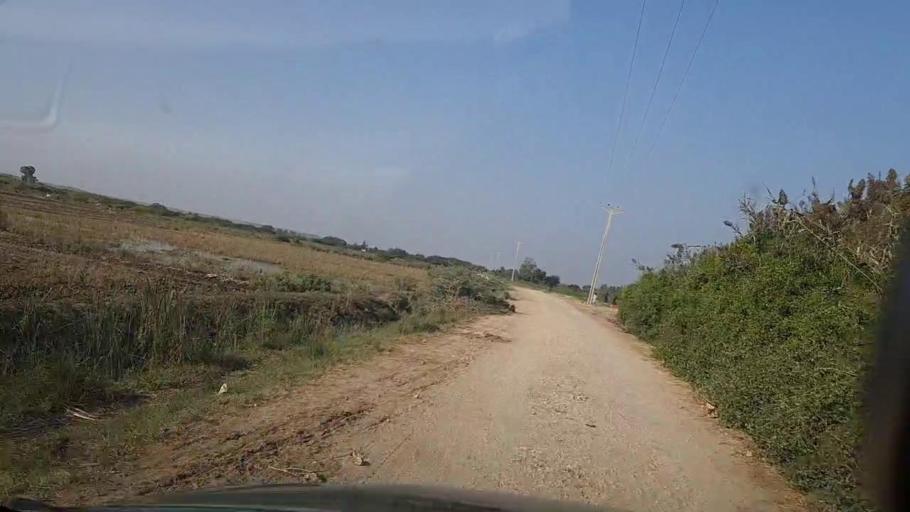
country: PK
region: Sindh
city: Thatta
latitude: 24.6042
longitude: 67.8744
